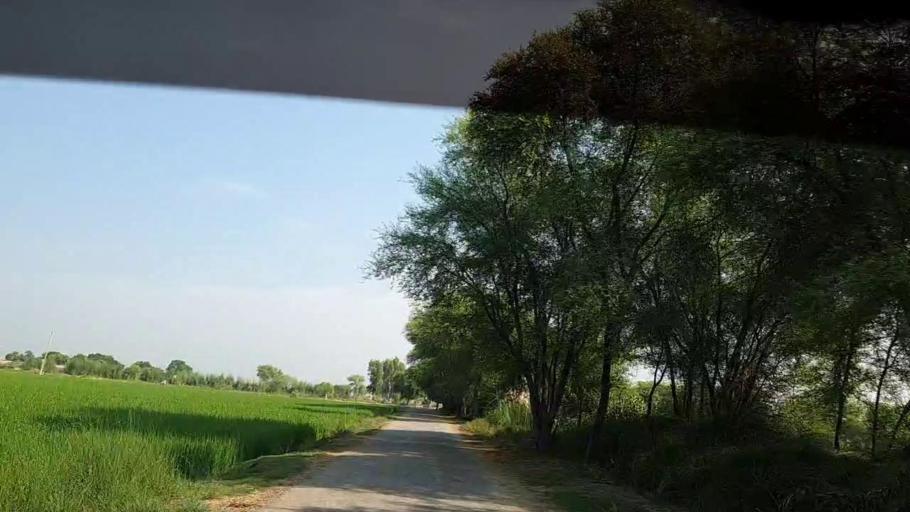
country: PK
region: Sindh
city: Shikarpur
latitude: 28.0926
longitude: 68.6769
